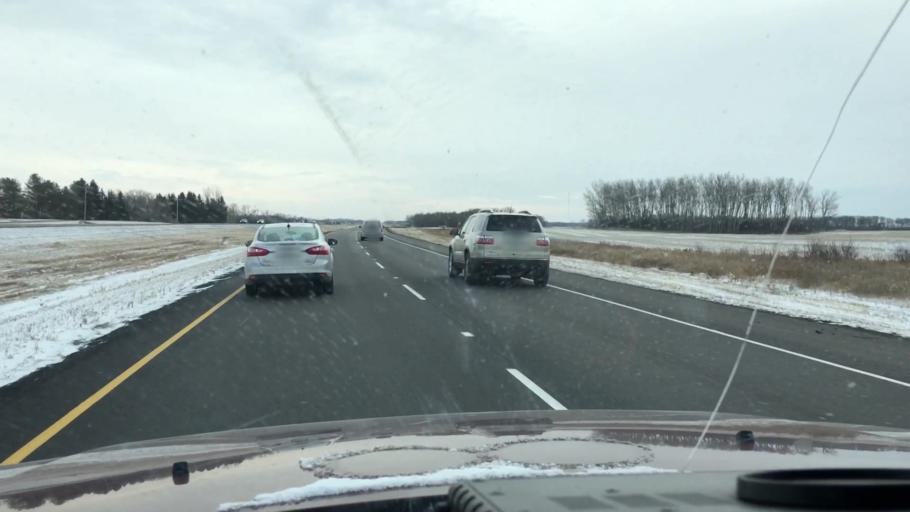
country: CA
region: Saskatchewan
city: Saskatoon
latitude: 52.0171
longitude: -106.5761
